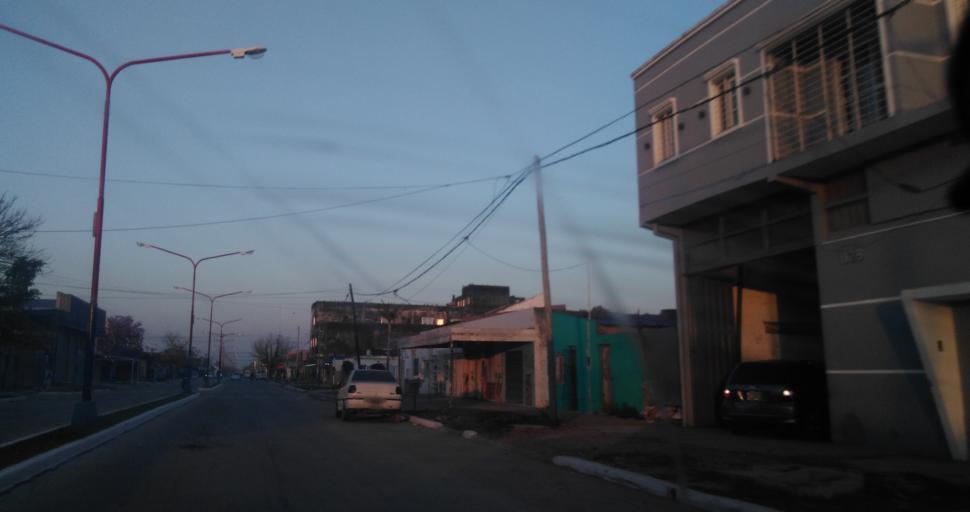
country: AR
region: Chaco
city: Resistencia
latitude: -27.4790
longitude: -58.9749
